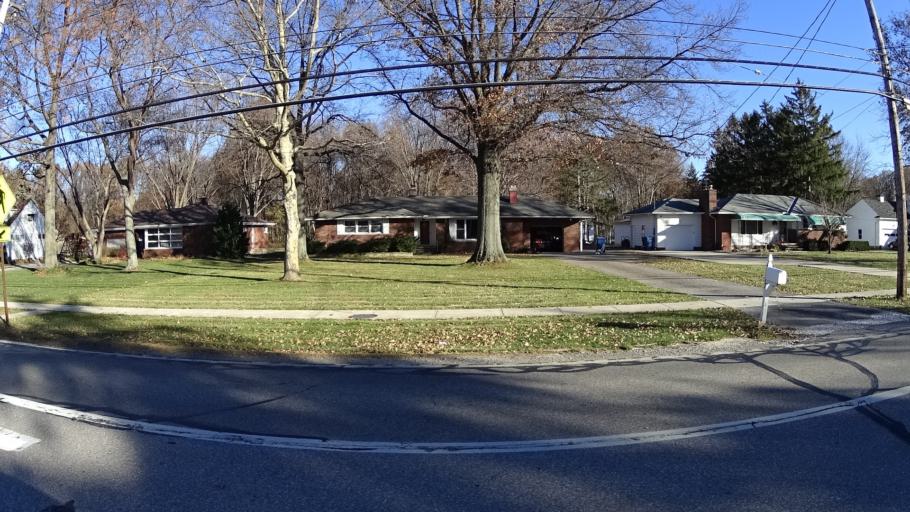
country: US
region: Ohio
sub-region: Lorain County
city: Avon Center
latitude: 41.4481
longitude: -82.0002
